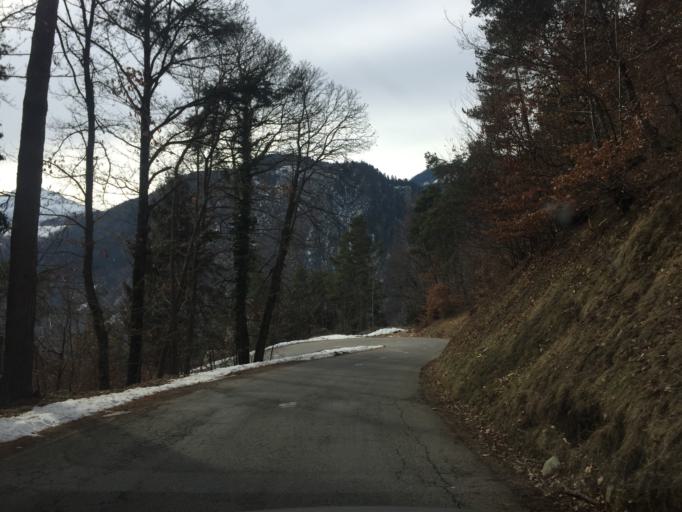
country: FR
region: Rhone-Alpes
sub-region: Departement de la Savoie
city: Aigueblanche
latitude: 45.5282
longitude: 6.4882
